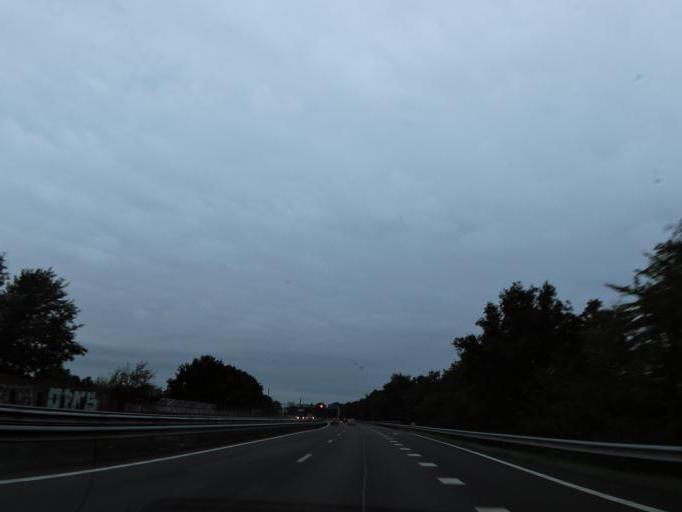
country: NL
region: Limburg
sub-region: Gemeente Maasgouw
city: Maasbracht
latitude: 51.1645
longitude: 5.8847
